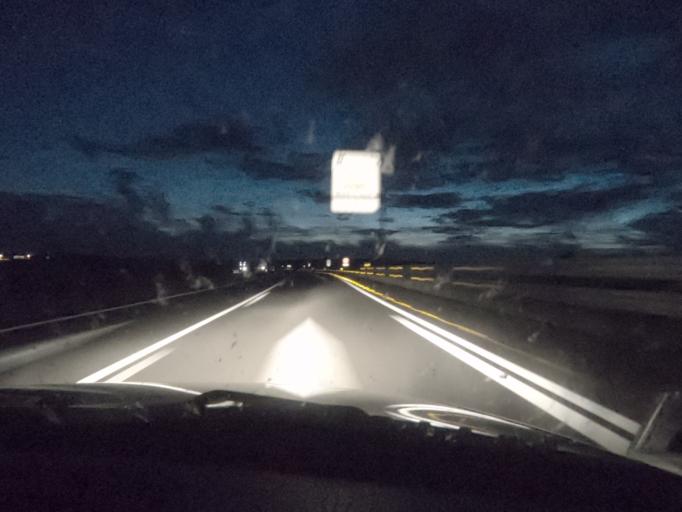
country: ES
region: Extremadura
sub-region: Provincia de Caceres
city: Morcillo
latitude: 39.9899
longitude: -6.4443
